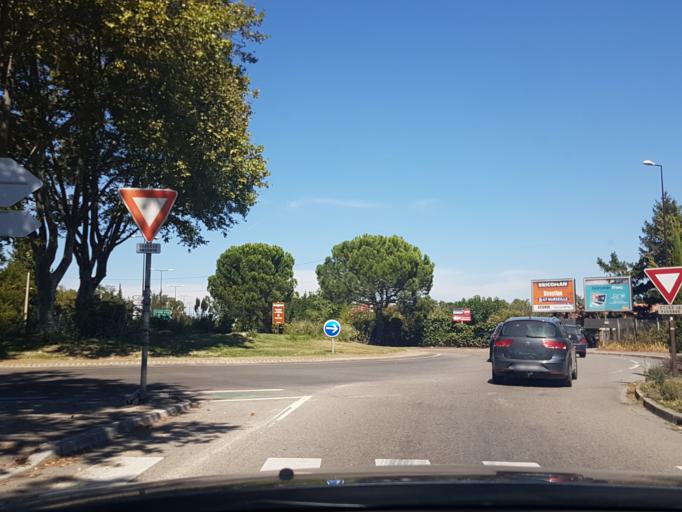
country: FR
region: Provence-Alpes-Cote d'Azur
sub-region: Departement des Bouches-du-Rhone
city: Rognonas
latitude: 43.9204
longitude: 4.8093
